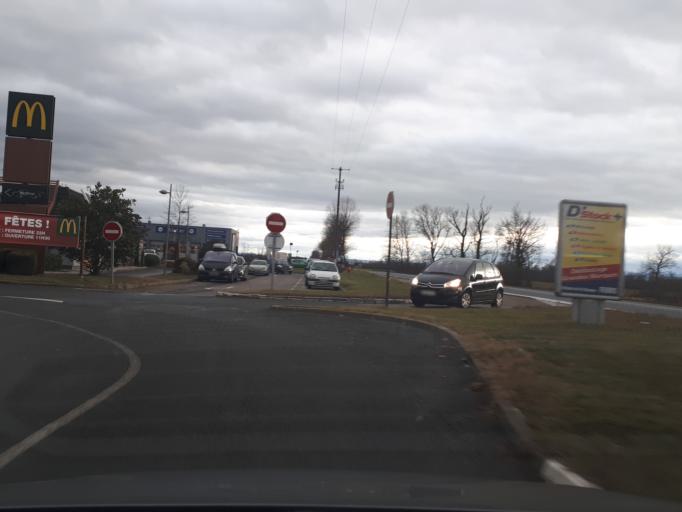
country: FR
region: Rhone-Alpes
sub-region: Departement de la Loire
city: Feurs
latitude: 45.7203
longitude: 4.2263
